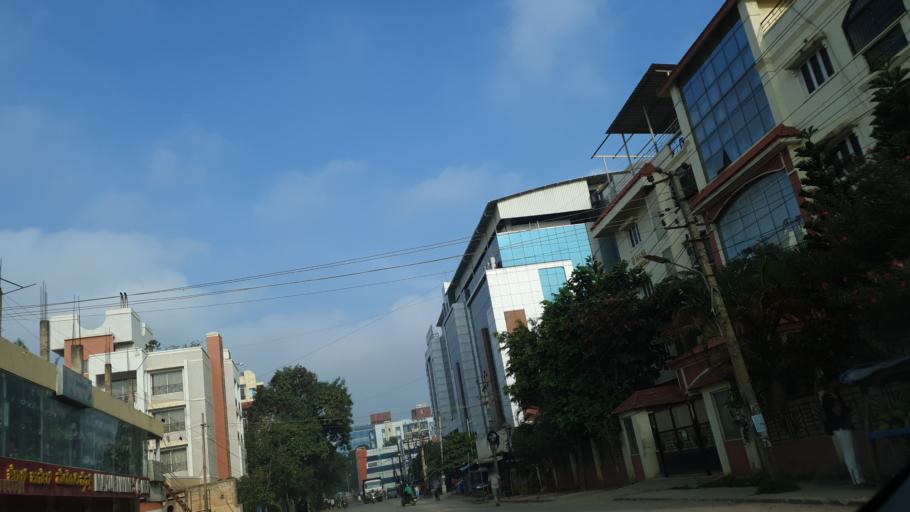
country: IN
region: Karnataka
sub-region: Bangalore Urban
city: Bangalore
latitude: 12.9388
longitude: 77.6967
